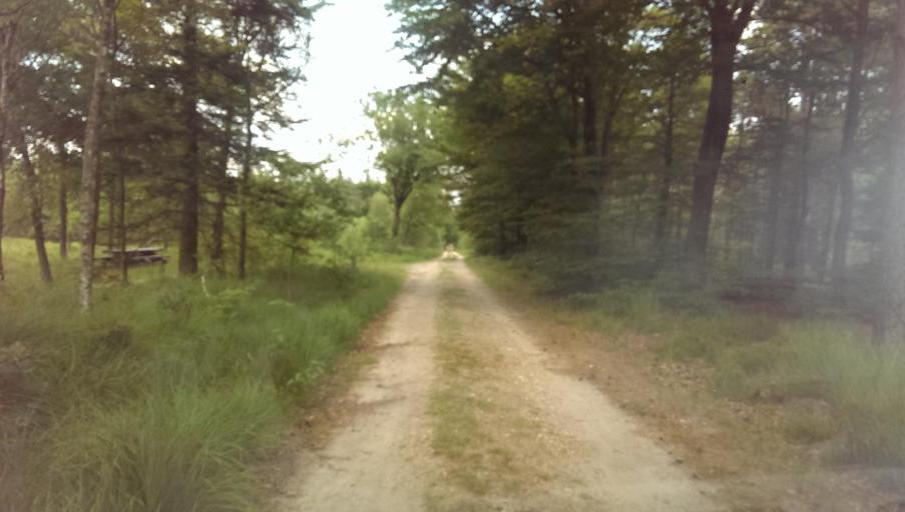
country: DK
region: South Denmark
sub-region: Varde Kommune
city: Varde
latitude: 55.5941
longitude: 8.5168
